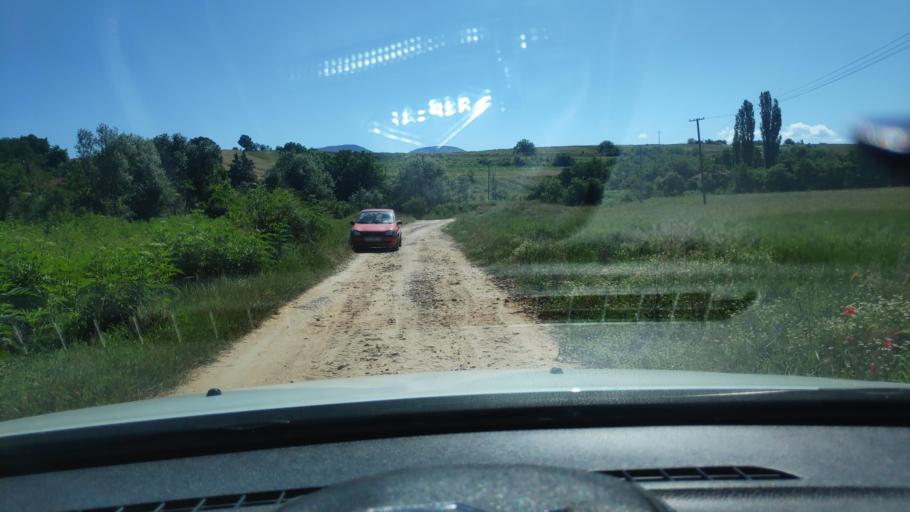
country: MK
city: Klechovce
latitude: 42.0654
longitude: 21.8564
